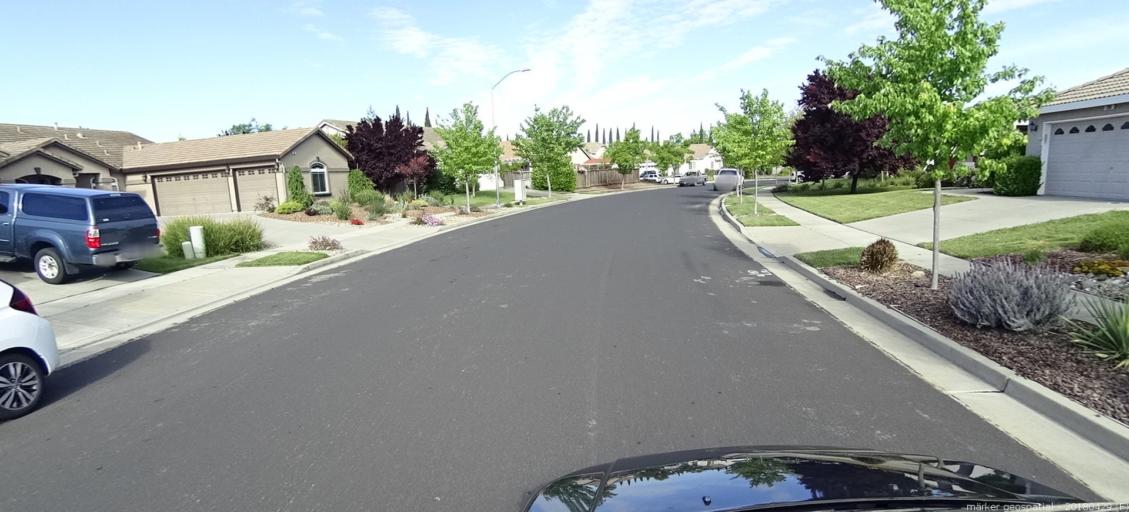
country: US
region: California
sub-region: Yolo County
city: West Sacramento
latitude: 38.5373
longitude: -121.5631
